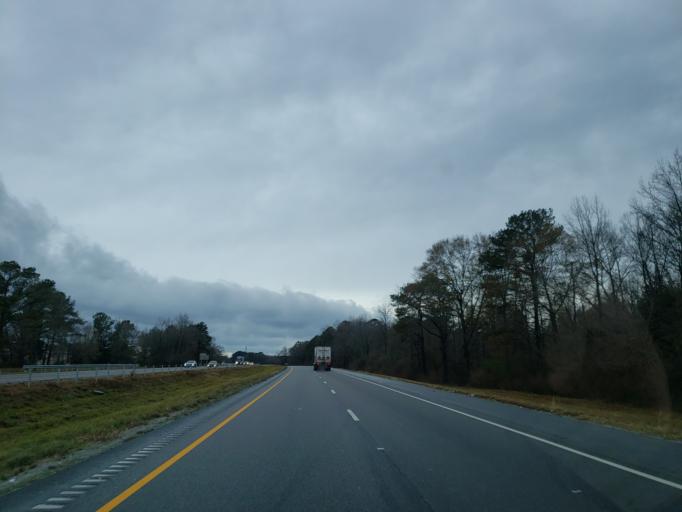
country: US
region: Alabama
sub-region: Talladega County
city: Lincoln
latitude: 33.5853
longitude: -86.0402
